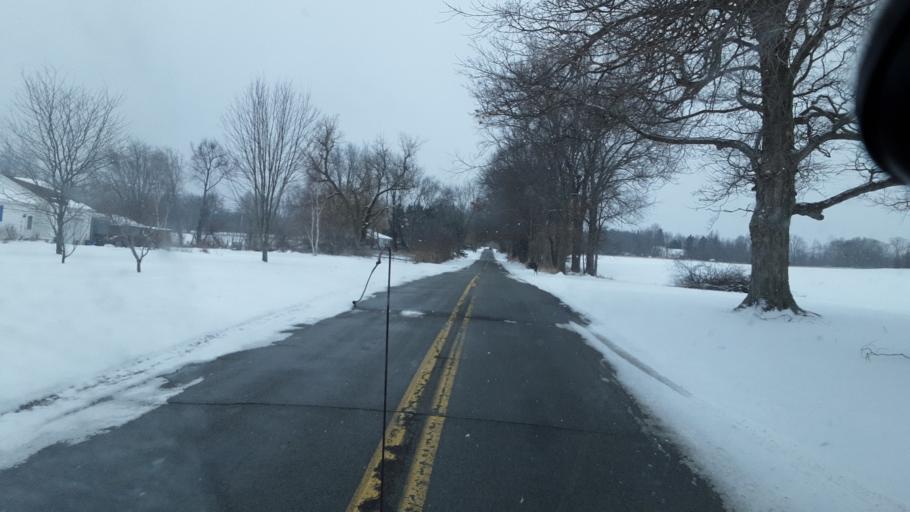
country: US
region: Michigan
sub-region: Ingham County
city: Leslie
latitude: 42.4272
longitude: -84.4775
